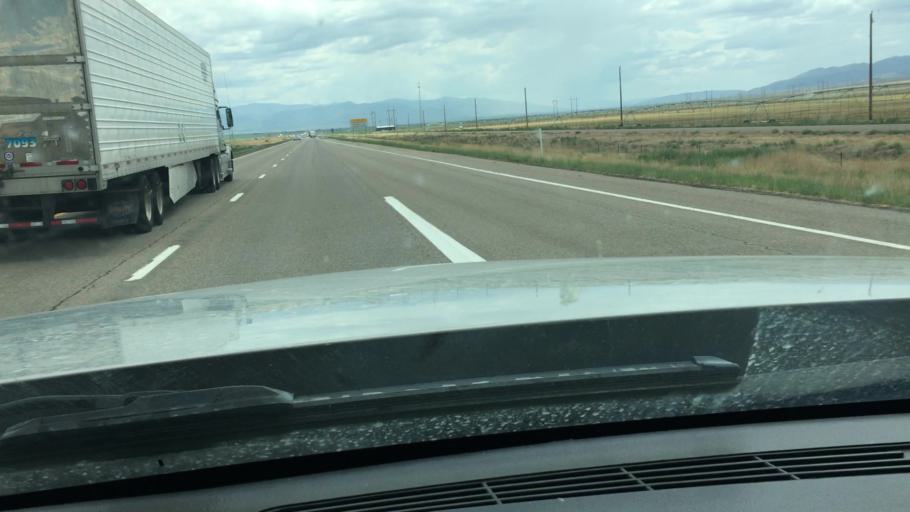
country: US
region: Utah
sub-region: Beaver County
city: Beaver
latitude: 38.0655
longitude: -112.6921
